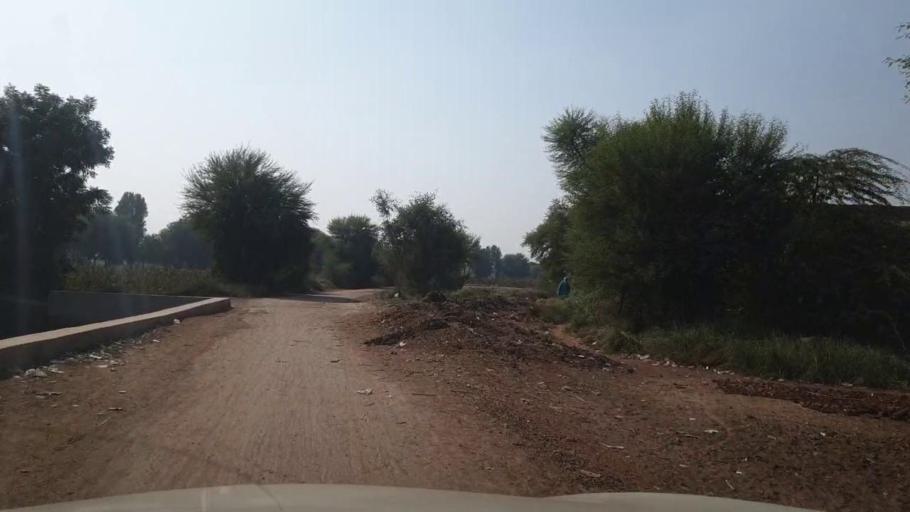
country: PK
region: Sindh
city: Bhan
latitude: 26.5156
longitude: 67.7770
